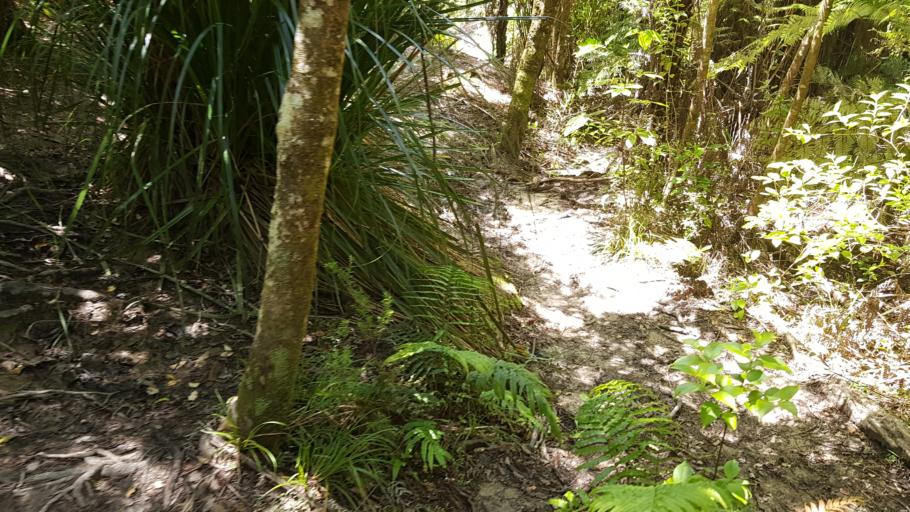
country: NZ
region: Auckland
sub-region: Auckland
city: North Shore
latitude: -36.8246
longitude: 174.7133
